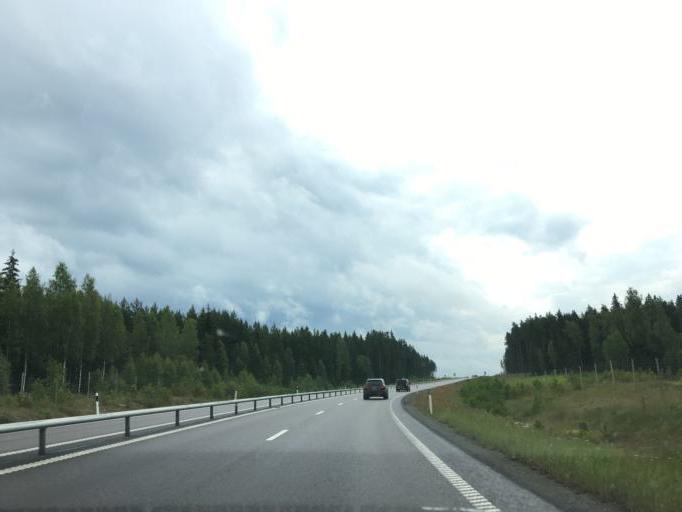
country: SE
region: Soedermanland
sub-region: Katrineholms Kommun
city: Katrineholm
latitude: 59.0056
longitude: 16.2439
